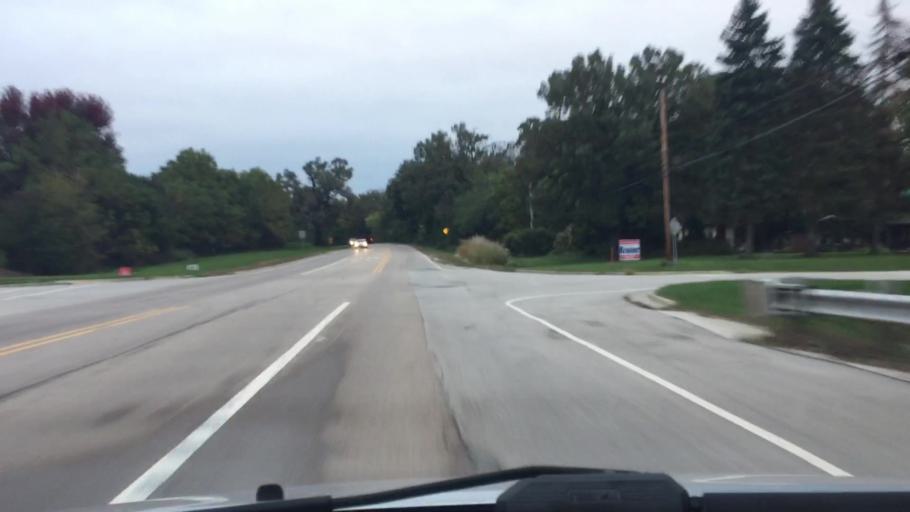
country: US
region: Illinois
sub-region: Kane County
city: South Elgin
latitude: 41.9804
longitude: -88.2971
